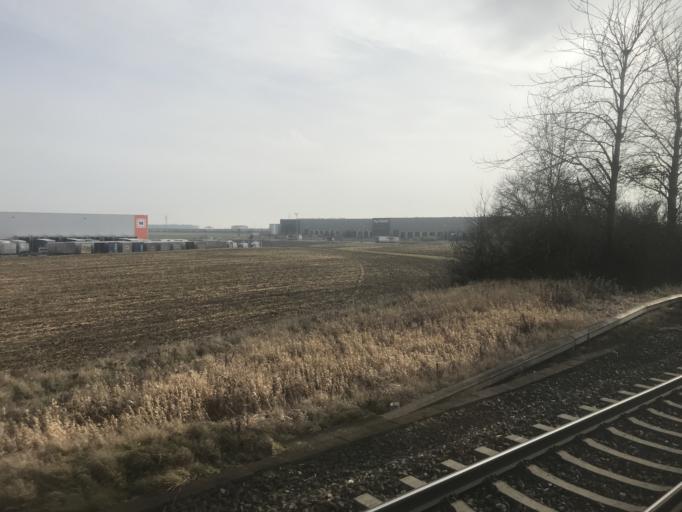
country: DE
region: Baden-Wuerttemberg
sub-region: Tuebingen Region
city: Beimerstetten
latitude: 48.4614
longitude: 9.9753
